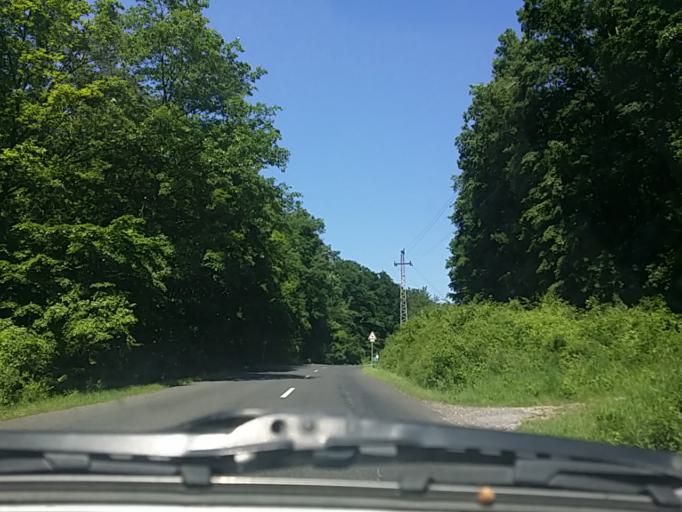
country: HU
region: Pest
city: Pilisszentkereszt
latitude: 47.7035
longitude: 18.8889
